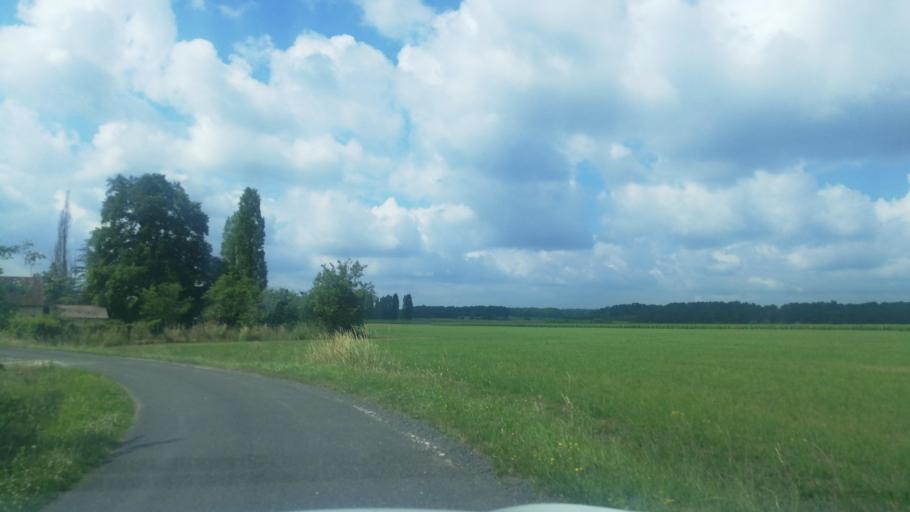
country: FR
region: Centre
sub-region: Departement du Loir-et-Cher
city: Saint-Romain-sur-Cher
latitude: 47.3651
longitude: 1.3953
